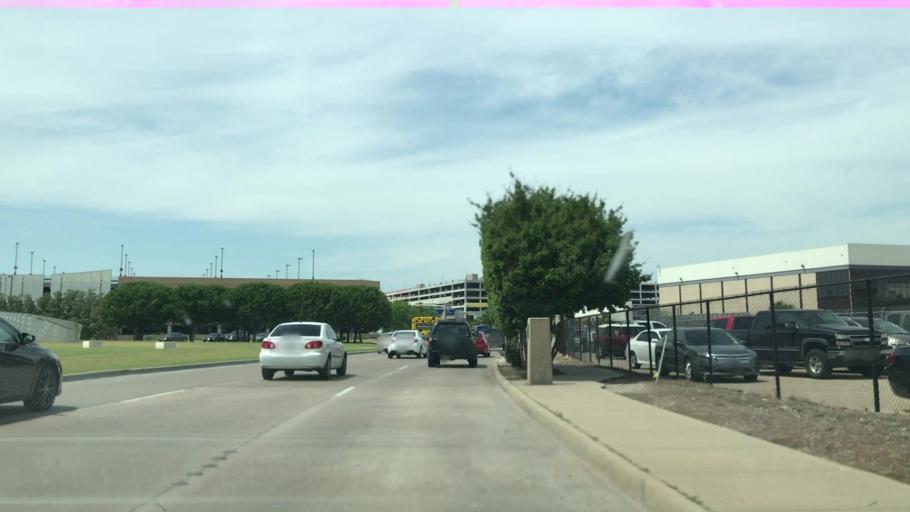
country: US
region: Texas
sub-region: Dallas County
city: University Park
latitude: 32.8395
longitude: -96.8452
